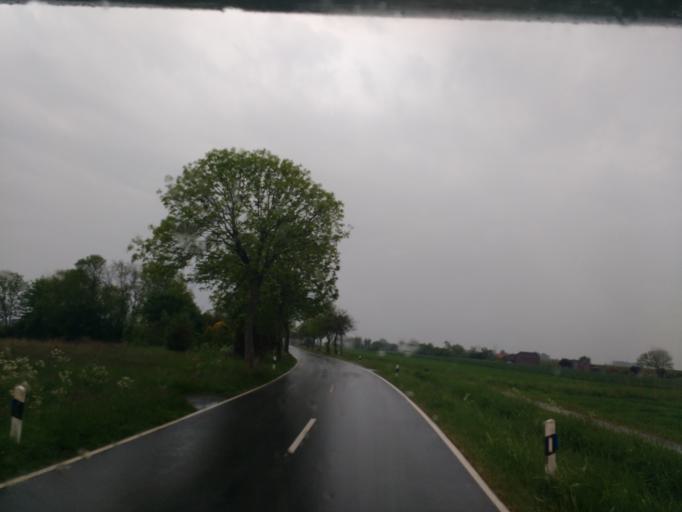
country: DE
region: Lower Saxony
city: Wangerooge
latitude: 53.7007
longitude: 7.9195
